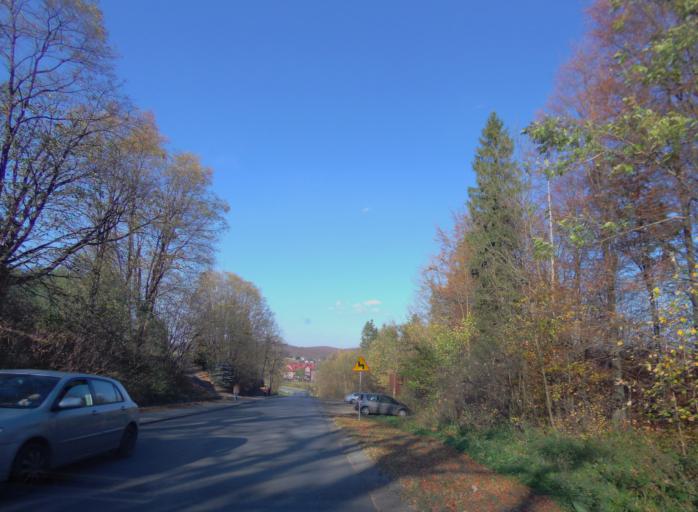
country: PL
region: Subcarpathian Voivodeship
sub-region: Powiat leski
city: Polanczyk
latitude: 49.3734
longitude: 22.4180
